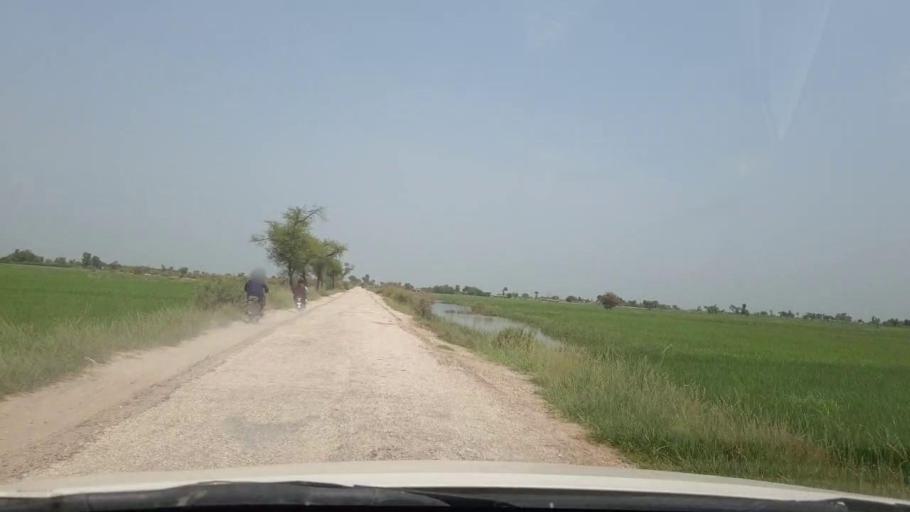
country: PK
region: Sindh
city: Rustam jo Goth
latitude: 28.0372
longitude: 68.8142
